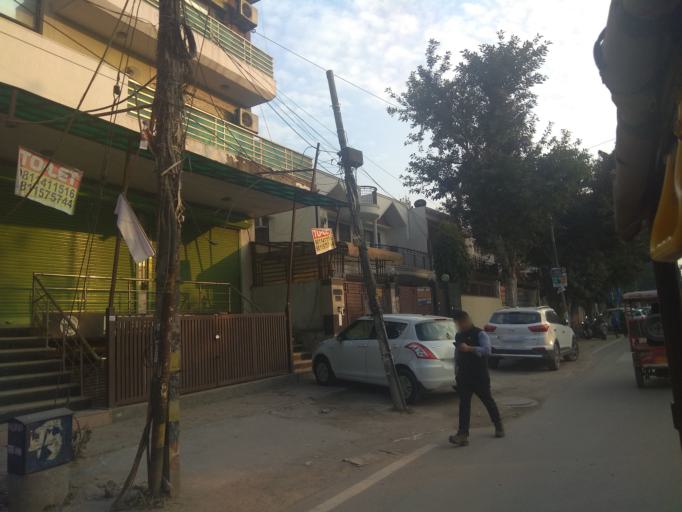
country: IN
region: NCT
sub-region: West Delhi
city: Nangloi Jat
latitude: 28.6327
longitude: 77.0688
